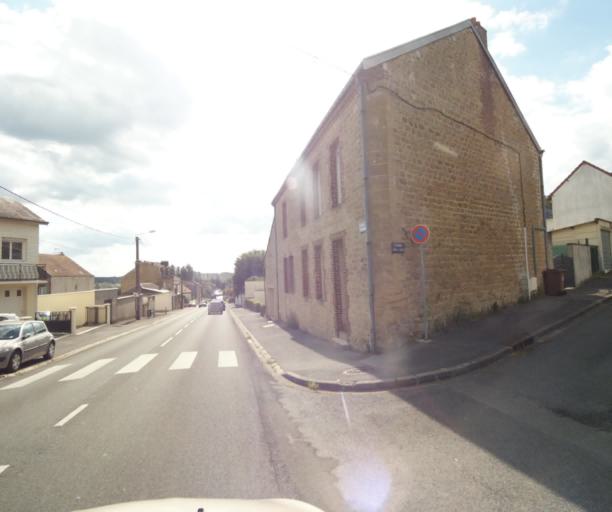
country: FR
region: Champagne-Ardenne
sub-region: Departement des Ardennes
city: Montcy-Notre-Dame
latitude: 49.7602
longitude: 4.7334
